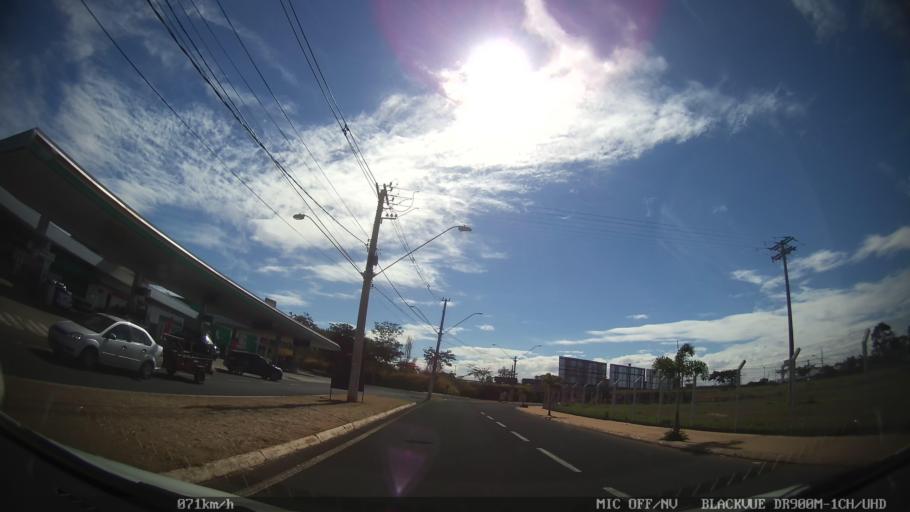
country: BR
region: Sao Paulo
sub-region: Sao Jose Do Rio Preto
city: Sao Jose do Rio Preto
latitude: -20.8138
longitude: -49.4813
